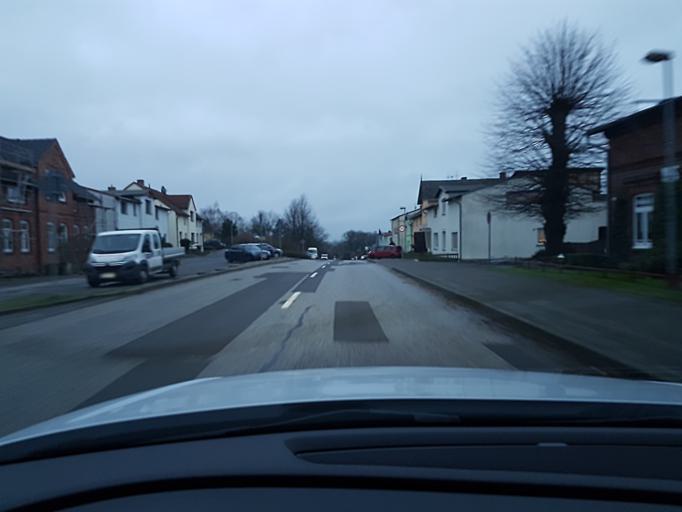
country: DE
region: Mecklenburg-Vorpommern
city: Satow-Oberhagen
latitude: 53.9879
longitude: 11.8849
